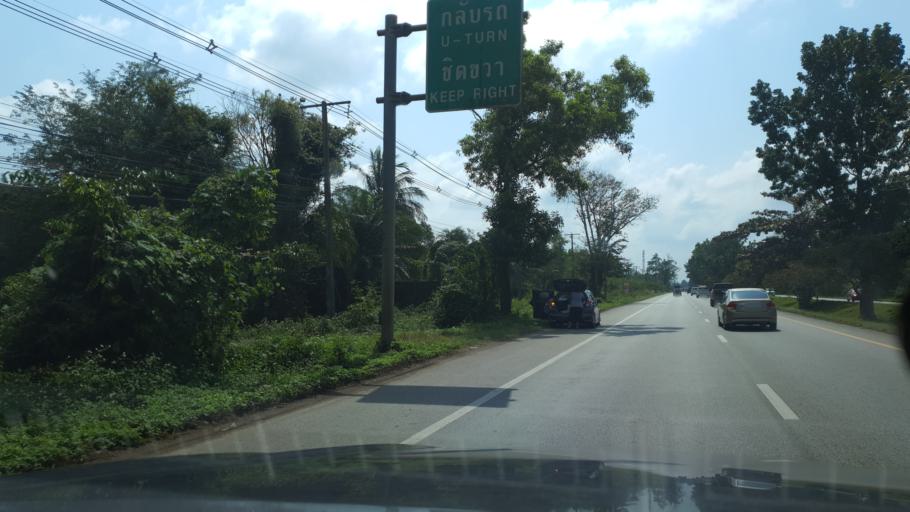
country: TH
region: Chumphon
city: Sawi
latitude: 10.1898
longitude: 99.0974
